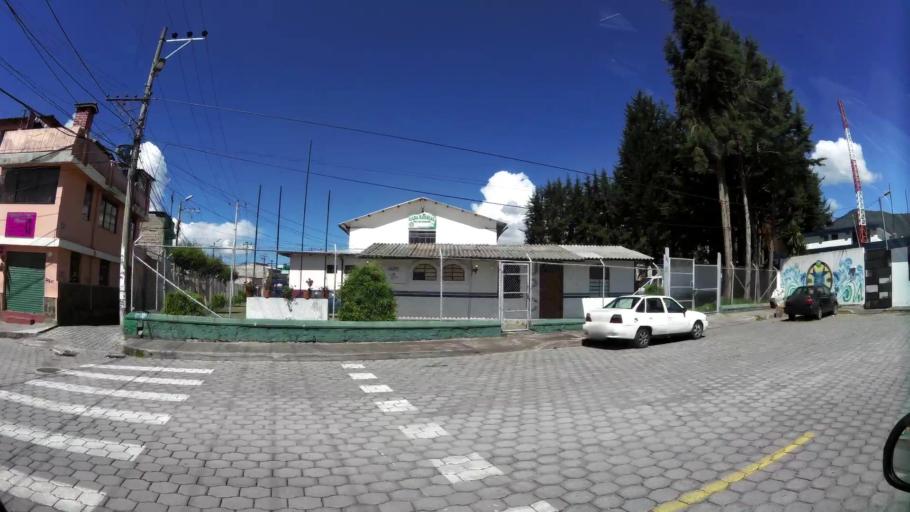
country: EC
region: Pichincha
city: Quito
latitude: -0.2547
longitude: -78.5376
